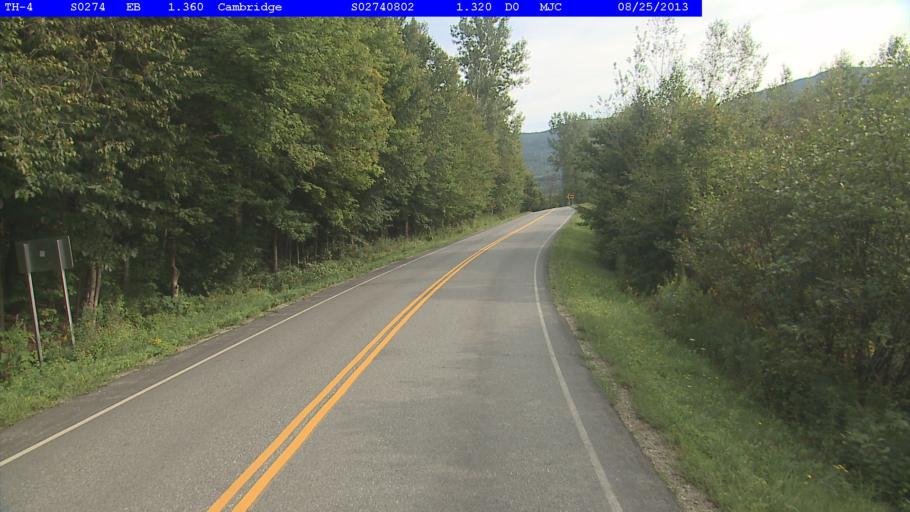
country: US
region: Vermont
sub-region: Lamoille County
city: Johnson
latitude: 44.6662
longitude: -72.7601
